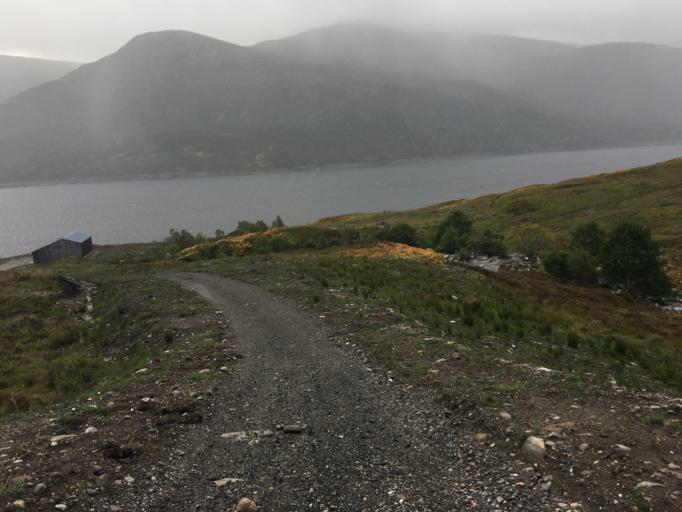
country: GB
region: Scotland
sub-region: Highland
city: Spean Bridge
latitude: 57.3430
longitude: -4.9824
